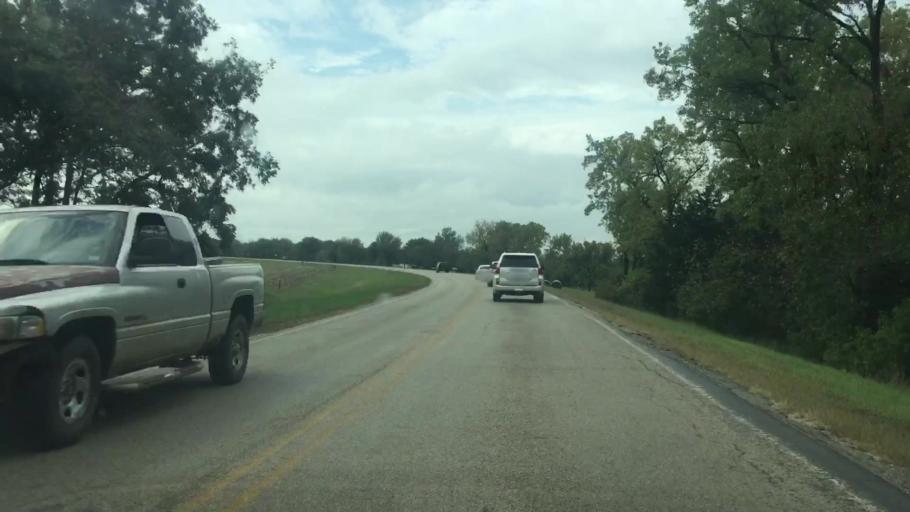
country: US
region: Kansas
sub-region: Allen County
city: Iola
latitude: 37.8826
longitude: -95.4348
